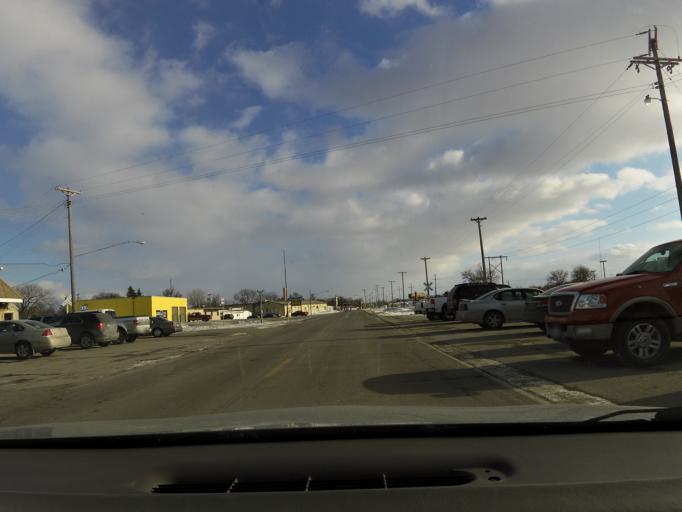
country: US
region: North Dakota
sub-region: Grand Forks County
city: Grand Forks
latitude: 47.9364
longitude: -97.0520
